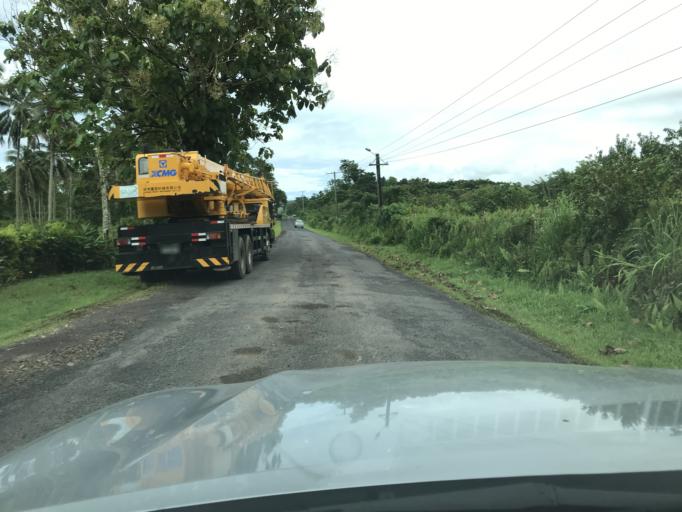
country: WS
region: A'ana
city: Satapuala
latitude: -13.8795
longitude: -171.9445
